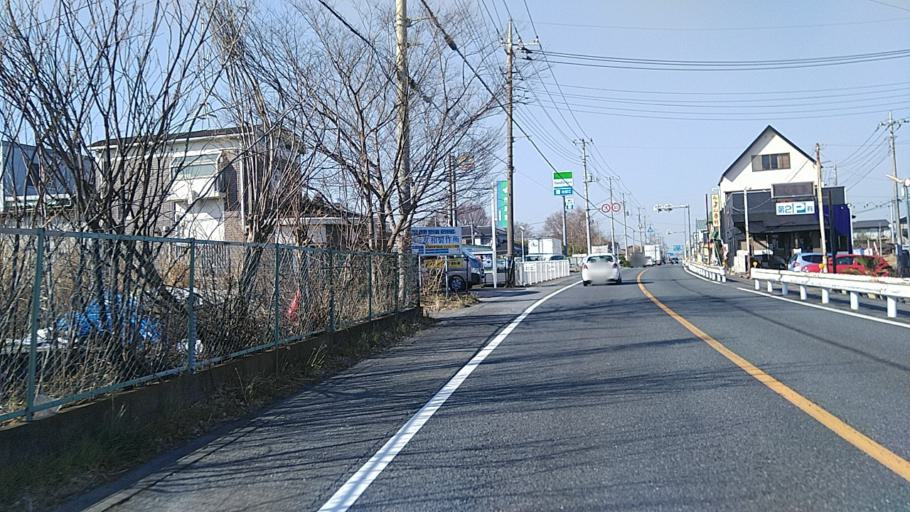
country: JP
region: Saitama
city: Fukiage-fujimi
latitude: 36.0708
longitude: 139.4076
